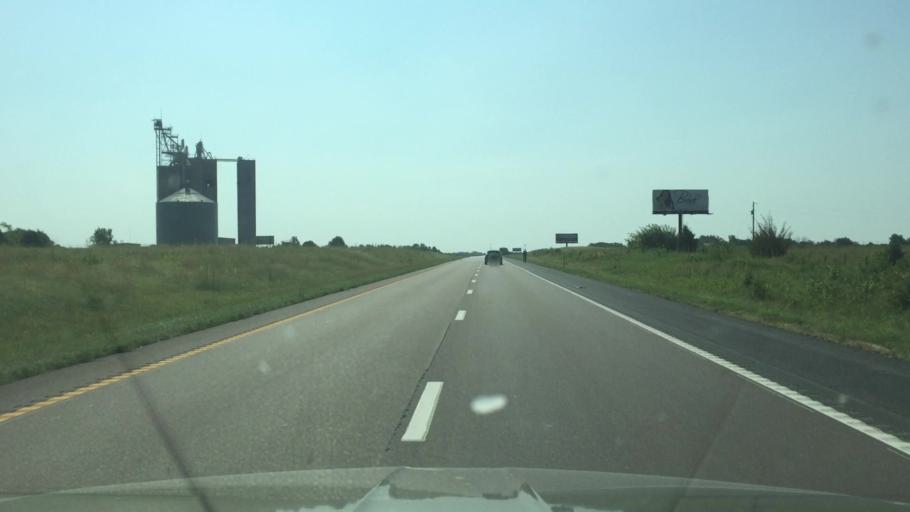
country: US
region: Missouri
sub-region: Pettis County
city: La Monte
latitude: 38.7515
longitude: -93.3512
